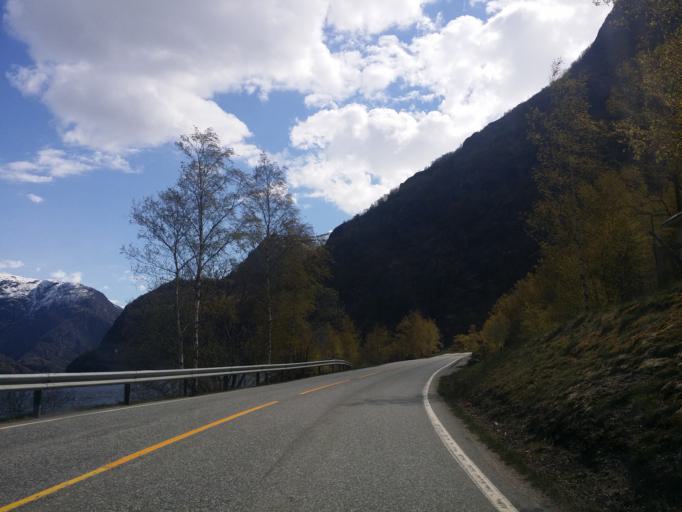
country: NO
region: Hordaland
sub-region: Eidfjord
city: Eidfjord
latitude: 60.4568
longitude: 7.0928
